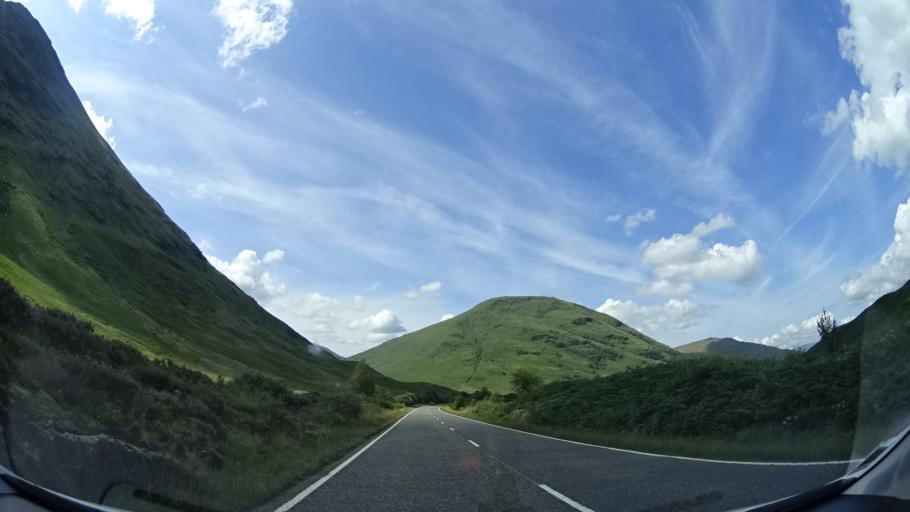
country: GB
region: Scotland
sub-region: Highland
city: Fort William
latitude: 56.6629
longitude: -5.0465
